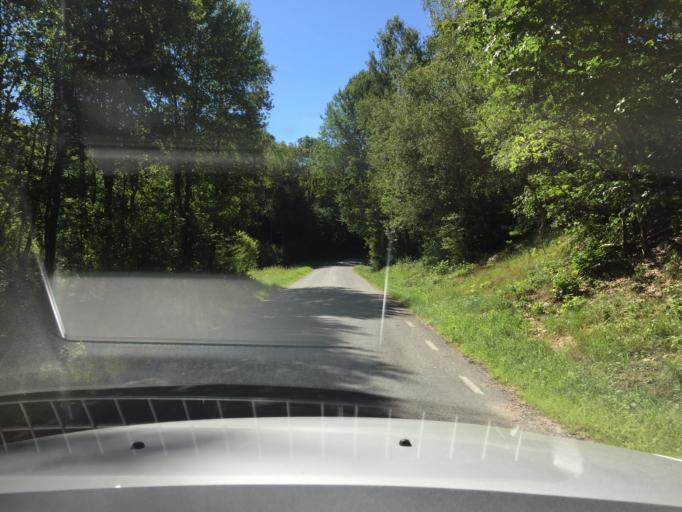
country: SE
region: Skane
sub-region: Hassleholms Kommun
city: Sosdala
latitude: 56.0222
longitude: 13.5816
